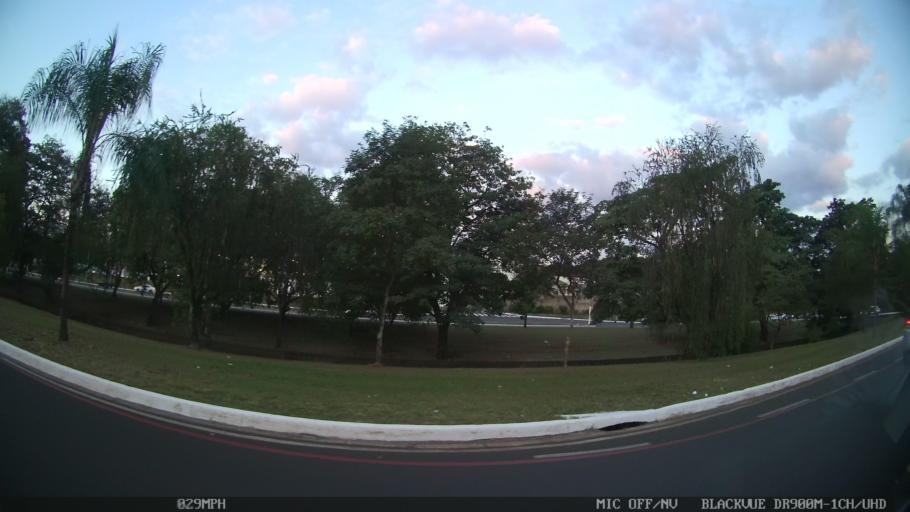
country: BR
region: Sao Paulo
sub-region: Ribeirao Preto
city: Ribeirao Preto
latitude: -21.1960
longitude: -47.7985
